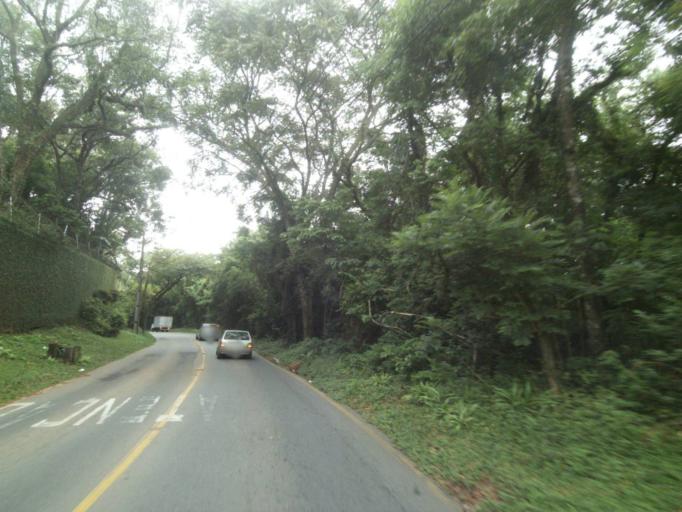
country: BR
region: Parana
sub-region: Curitiba
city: Curitiba
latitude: -25.4054
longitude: -49.3055
